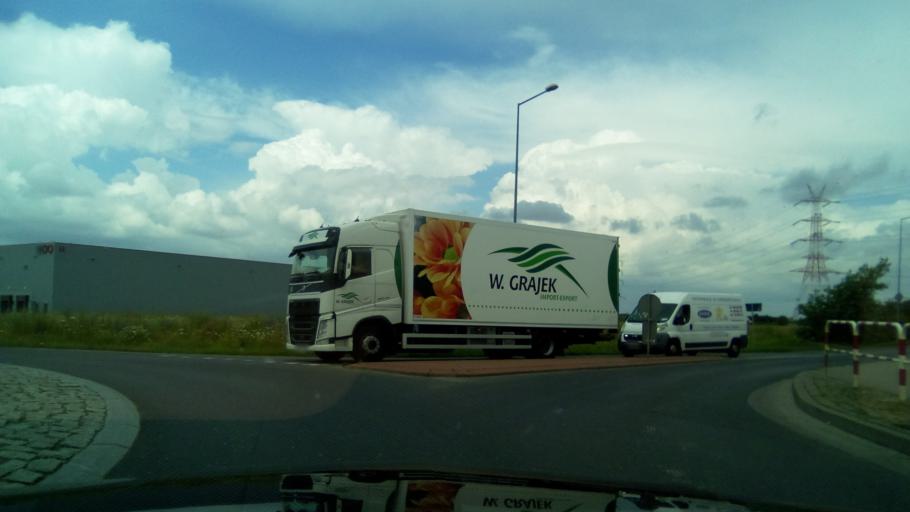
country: PL
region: Greater Poland Voivodeship
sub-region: Powiat poznanski
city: Komorniki
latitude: 52.3478
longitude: 16.8037
